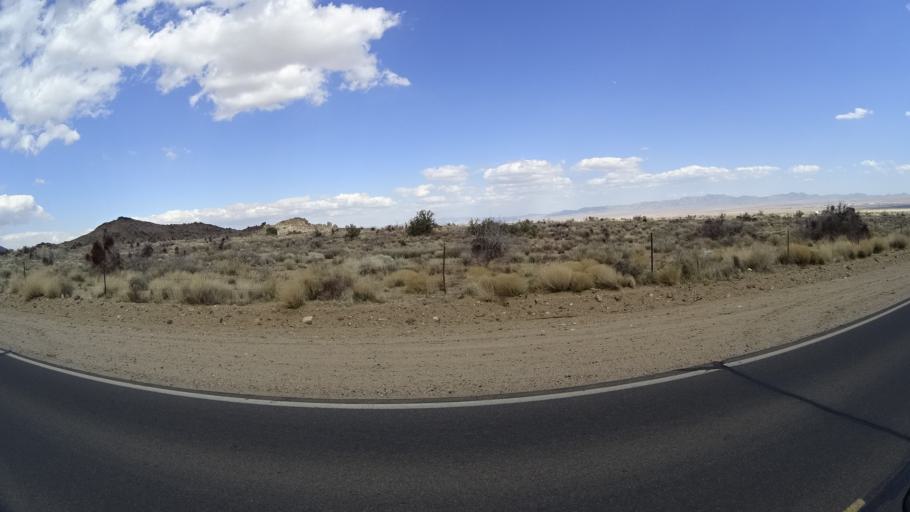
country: US
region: Arizona
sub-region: Mohave County
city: New Kingman-Butler
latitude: 35.2864
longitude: -114.0564
